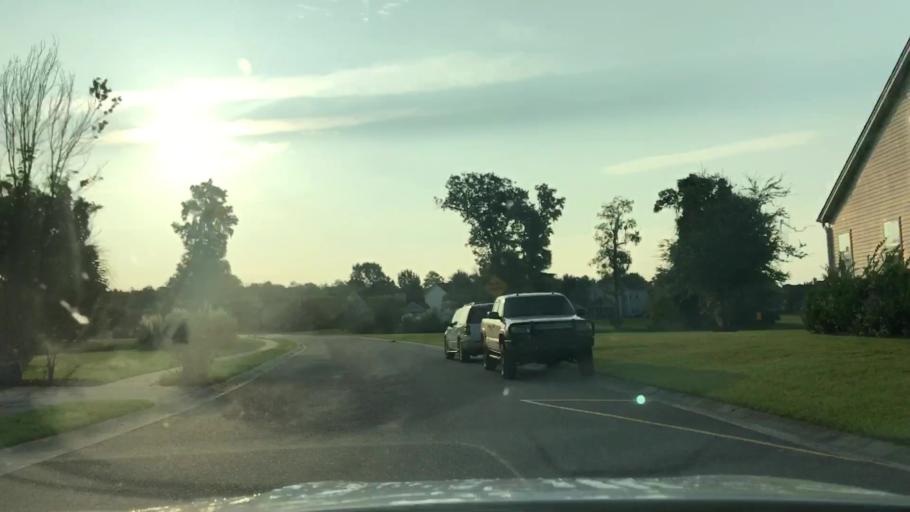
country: US
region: South Carolina
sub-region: Charleston County
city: Shell Point
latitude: 32.8362
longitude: -80.0944
